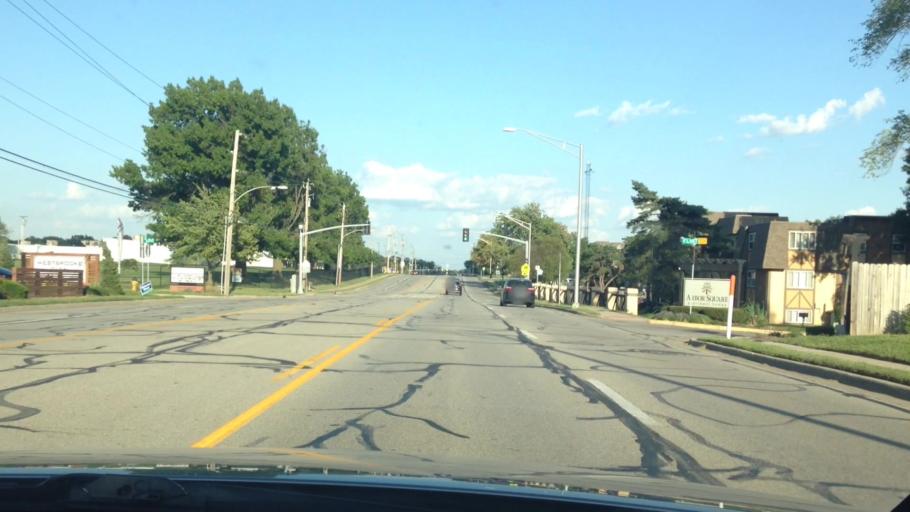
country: US
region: Kansas
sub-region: Johnson County
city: Merriam
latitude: 38.9928
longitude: -94.7193
